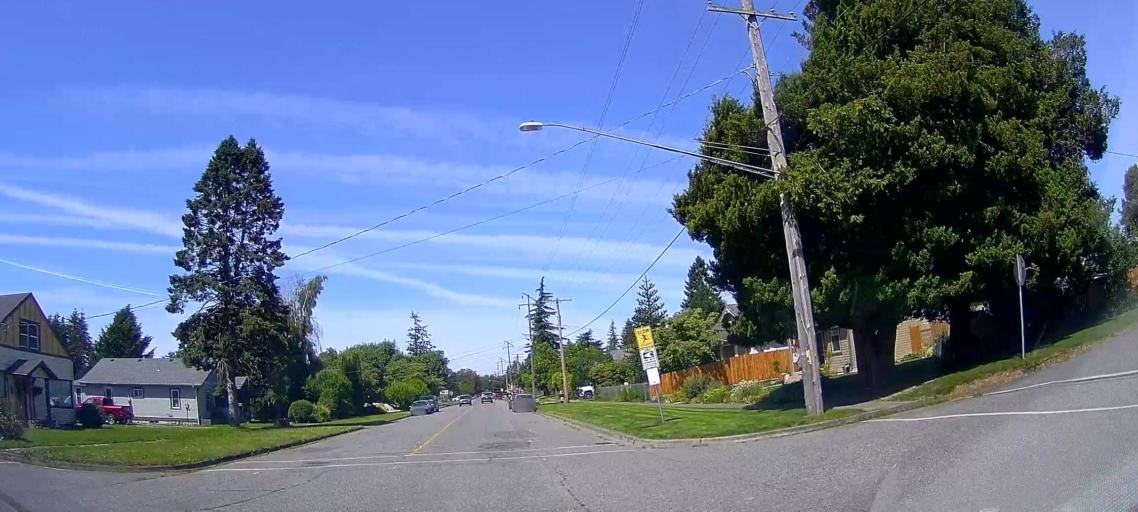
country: US
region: Washington
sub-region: Skagit County
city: Sedro-Woolley
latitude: 48.4989
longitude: -122.2278
